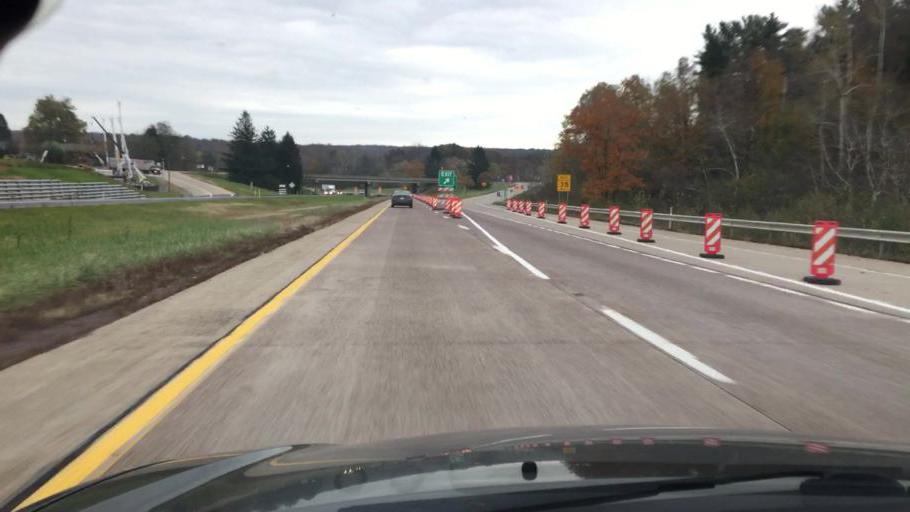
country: US
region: Pennsylvania
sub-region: Luzerne County
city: White Haven
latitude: 41.0561
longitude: -75.7801
